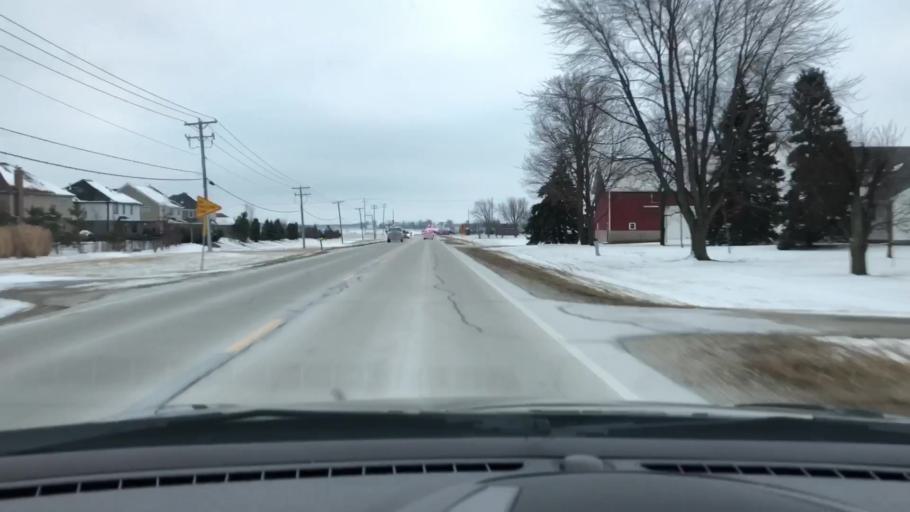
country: US
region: Illinois
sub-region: Will County
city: New Lenox
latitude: 41.4862
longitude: -88.0034
